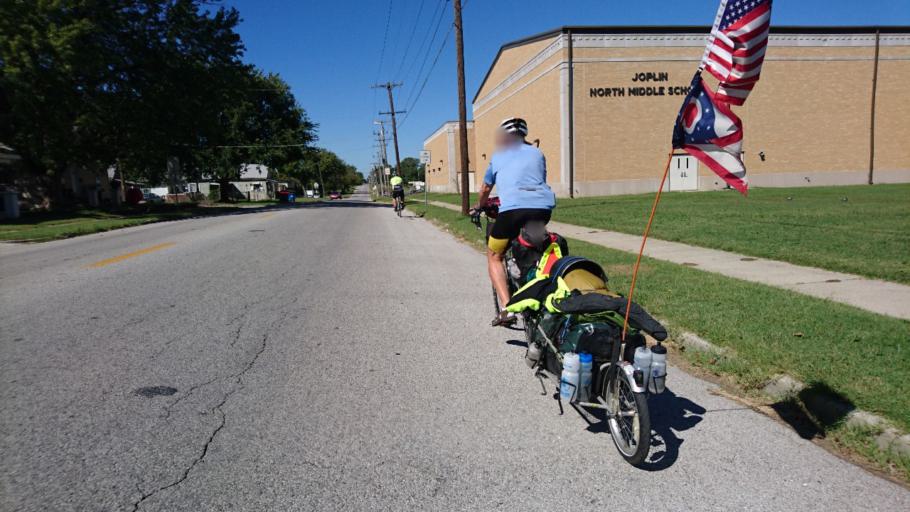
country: US
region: Missouri
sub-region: Jasper County
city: Joplin
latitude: 37.0900
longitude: -94.5243
